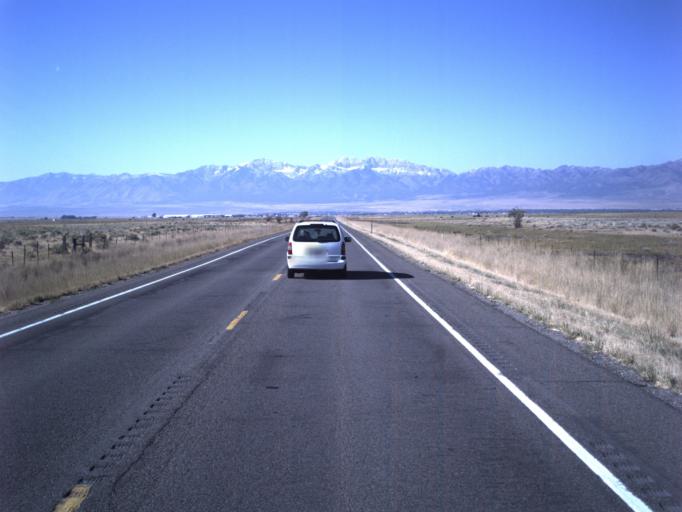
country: US
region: Utah
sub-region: Tooele County
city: Erda
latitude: 40.6314
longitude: -112.3379
